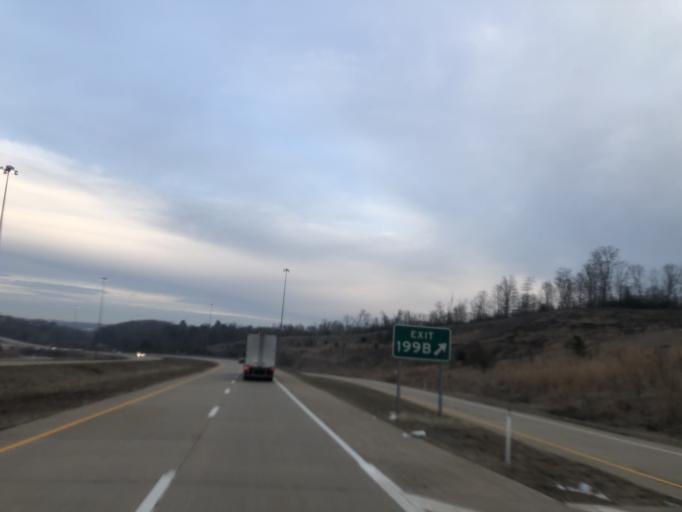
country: US
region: Ohio
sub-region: Athens County
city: Athens
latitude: 39.2976
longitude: -82.1028
